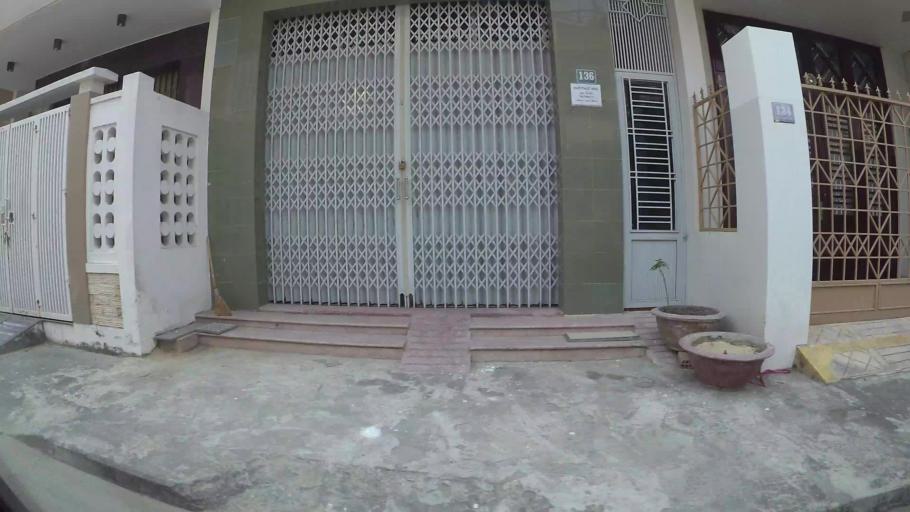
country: VN
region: Da Nang
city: Son Tra
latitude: 16.0434
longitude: 108.2220
